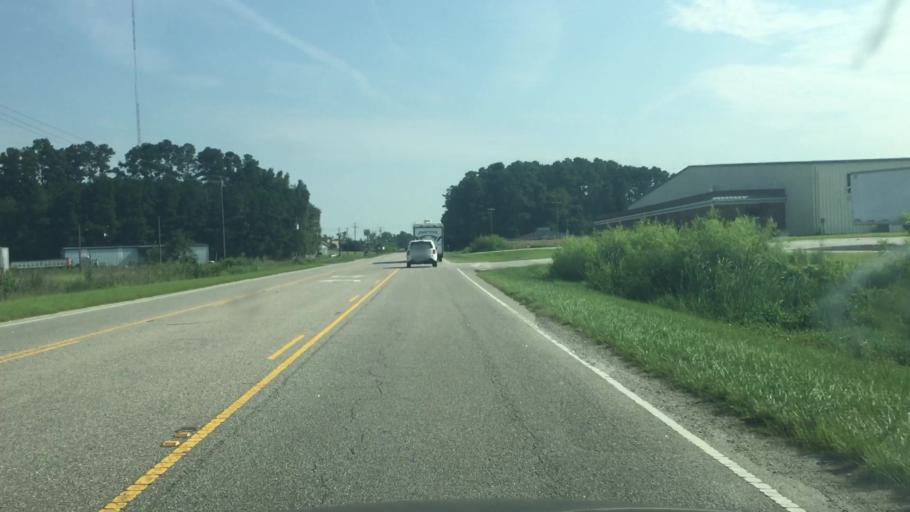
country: US
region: North Carolina
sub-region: Columbus County
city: Tabor City
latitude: 34.1502
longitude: -78.8614
